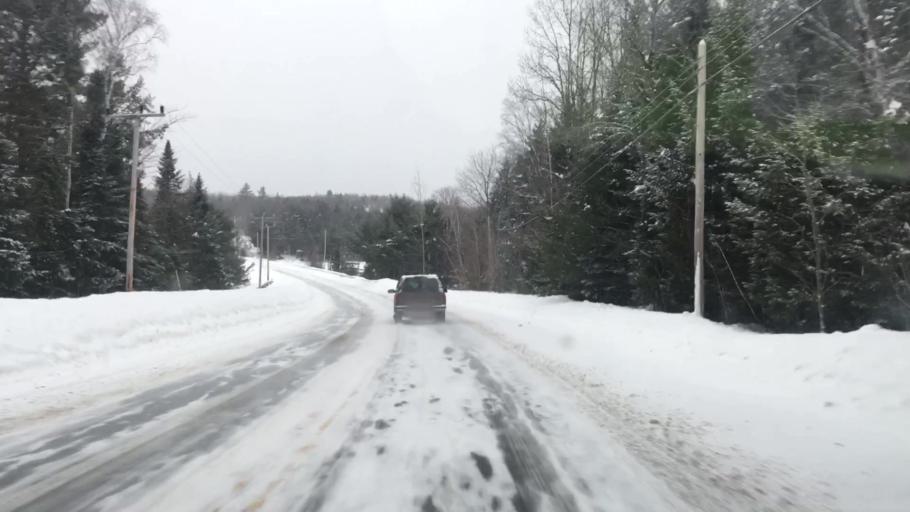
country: US
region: Maine
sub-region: Penobscot County
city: Medway
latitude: 45.6003
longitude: -68.4654
